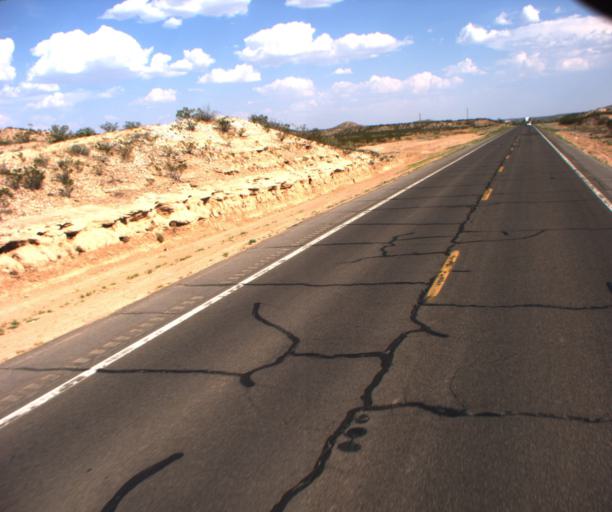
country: US
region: Arizona
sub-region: Greenlee County
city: Clifton
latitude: 32.7787
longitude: -109.1567
